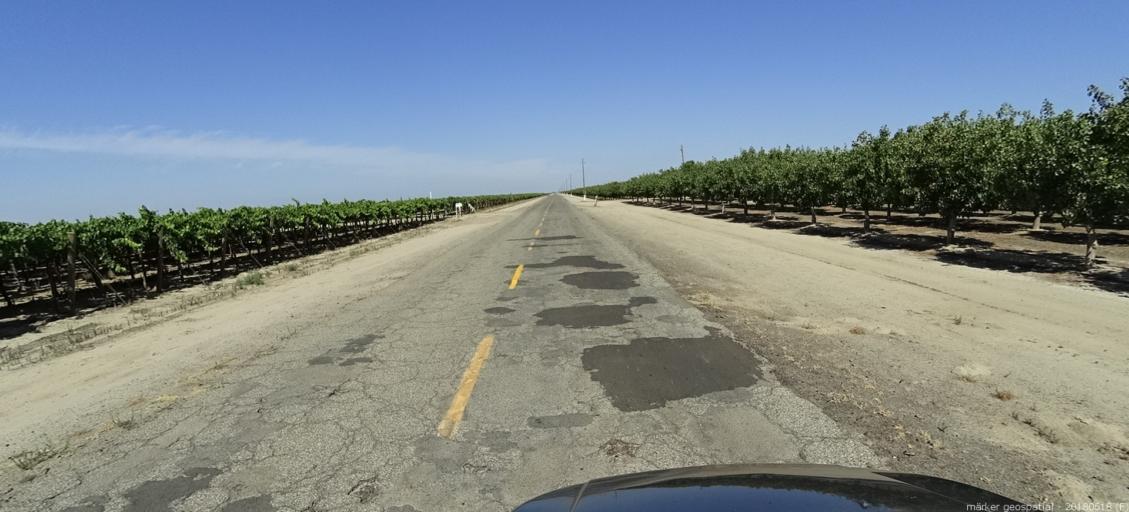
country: US
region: California
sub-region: Fresno County
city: Mendota
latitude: 36.8366
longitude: -120.2358
